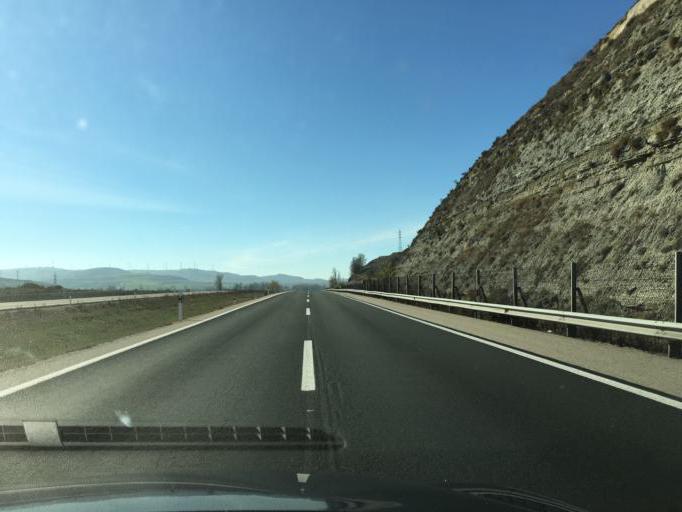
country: ES
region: Castille and Leon
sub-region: Provincia de Burgos
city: Castil de Peones
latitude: 42.4943
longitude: -3.3728
